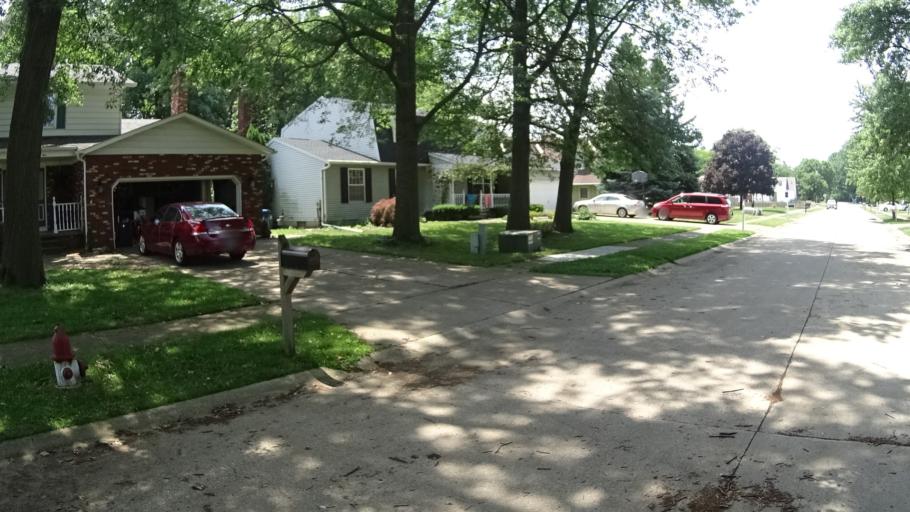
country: US
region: Ohio
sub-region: Lorain County
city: Vermilion
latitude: 41.4127
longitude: -82.3635
